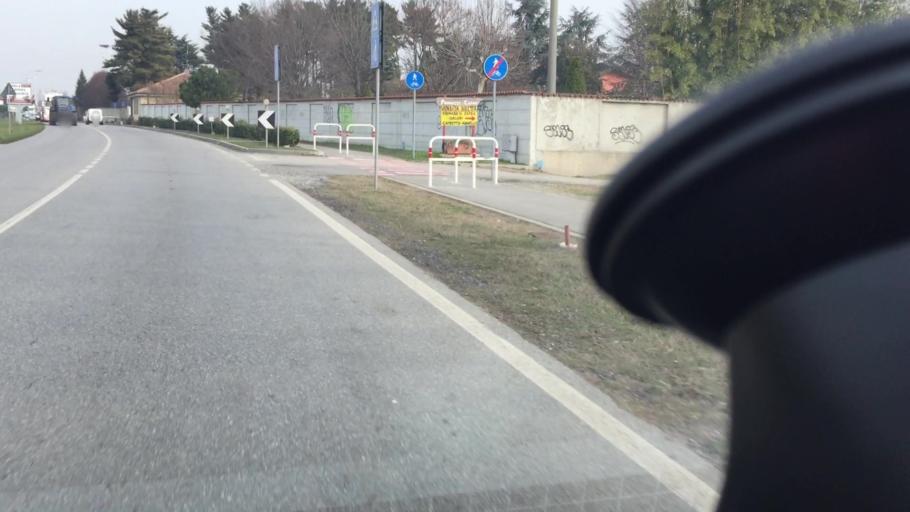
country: IT
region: Lombardy
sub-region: Citta metropolitana di Milano
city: Vaprio d'Adda
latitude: 45.5622
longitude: 9.5193
